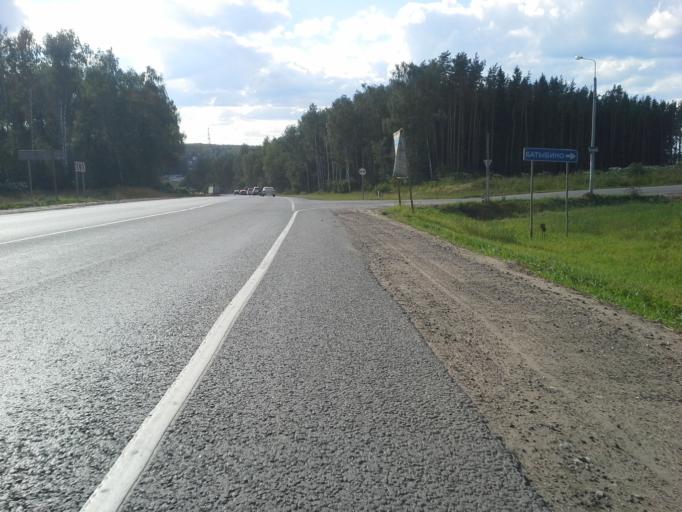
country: RU
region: Moskovskaya
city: Dubrovitsy
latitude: 55.3717
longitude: 37.4175
